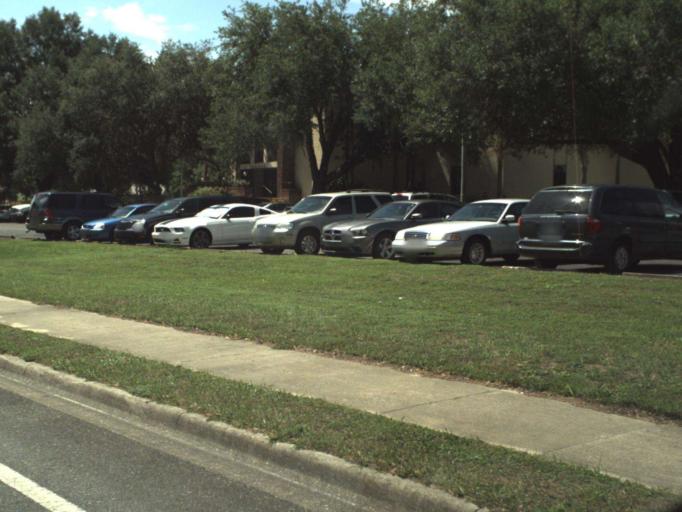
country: US
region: Florida
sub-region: Marion County
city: Ocala
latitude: 29.2007
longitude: -82.1121
